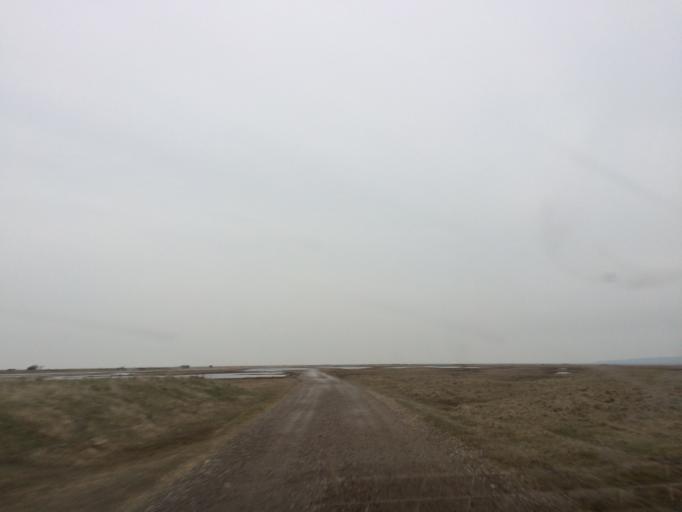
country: DK
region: Central Jutland
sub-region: Lemvig Kommune
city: Lemvig
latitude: 56.5881
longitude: 8.2902
